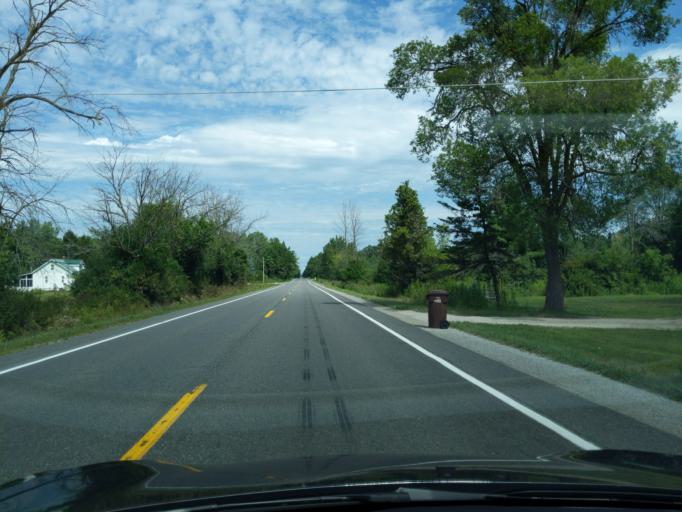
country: US
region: Michigan
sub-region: Midland County
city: Midland
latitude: 43.5804
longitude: -84.3696
